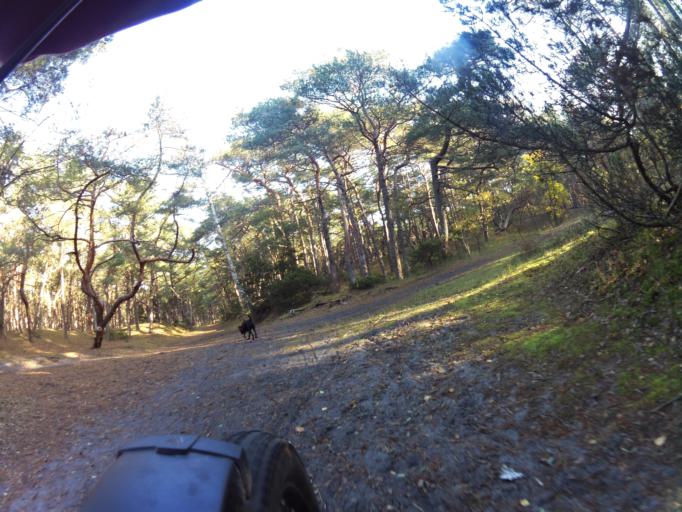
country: PL
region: Pomeranian Voivodeship
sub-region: Powiat pucki
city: Hel
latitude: 54.5984
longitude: 18.8137
